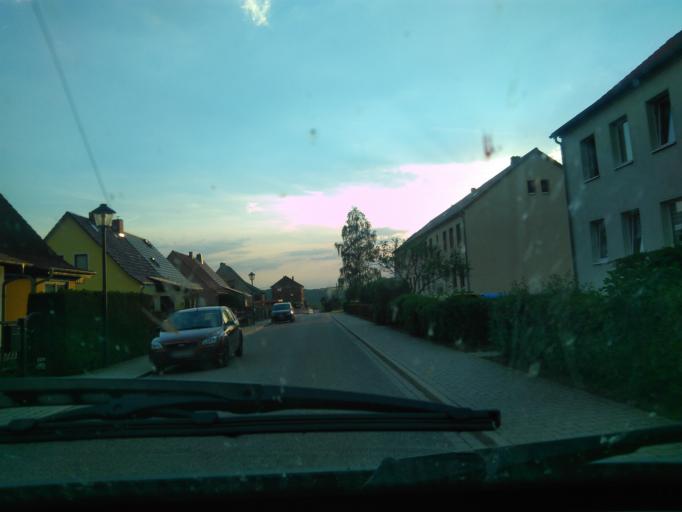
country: DE
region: Saxony-Anhalt
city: Wethau
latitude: 51.1216
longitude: 11.8791
